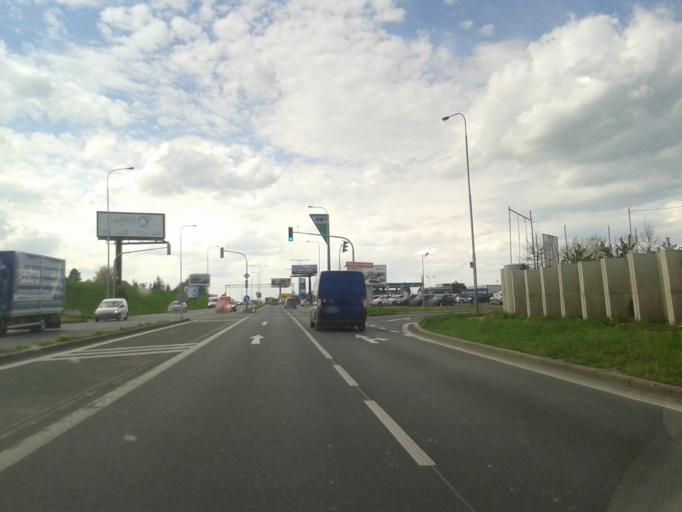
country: CZ
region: Praha
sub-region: Praha 12
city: Modrany
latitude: 50.0260
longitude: 14.3678
